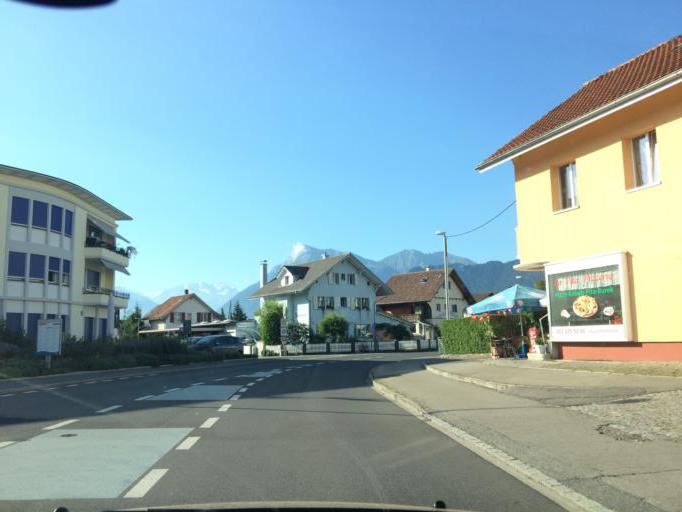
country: CH
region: Bern
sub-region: Thun District
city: Thun
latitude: 46.7416
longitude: 7.6147
